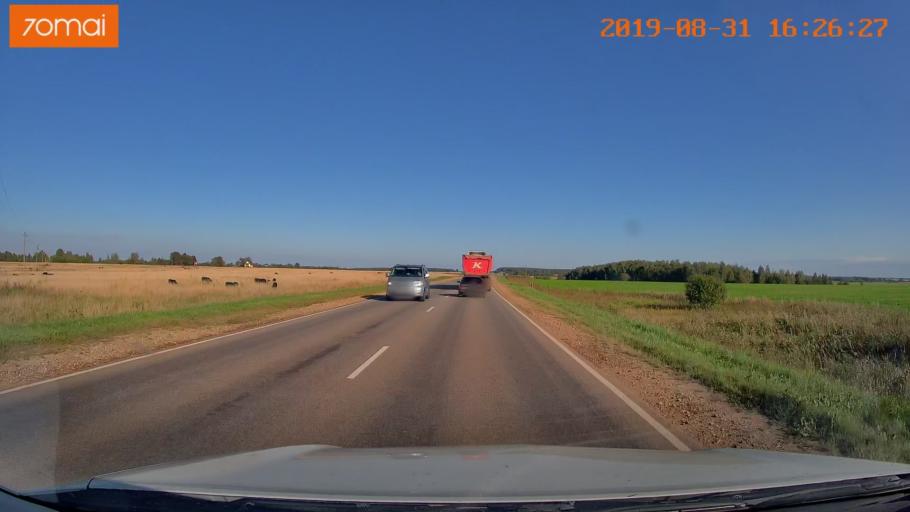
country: RU
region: Kaluga
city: Babynino
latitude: 54.5180
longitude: 35.7353
